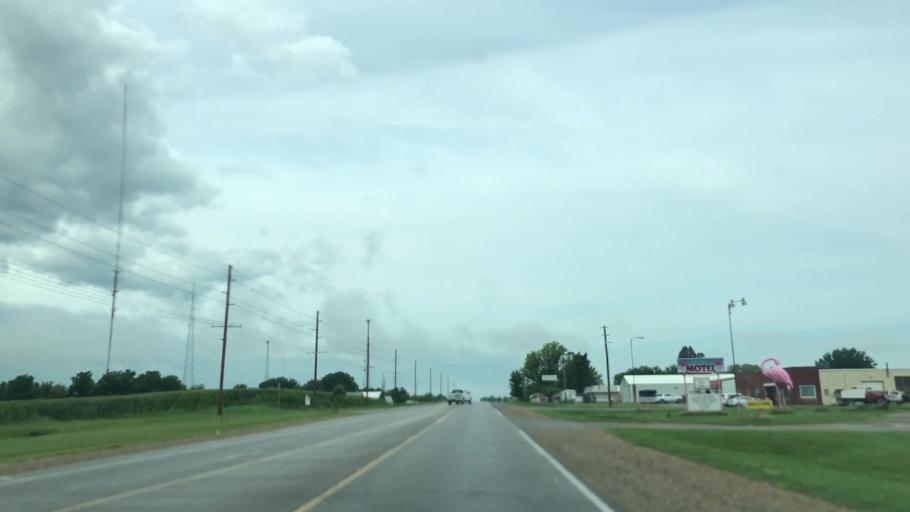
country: US
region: Iowa
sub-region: Marshall County
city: Marshalltown
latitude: 42.0072
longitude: -92.9236
